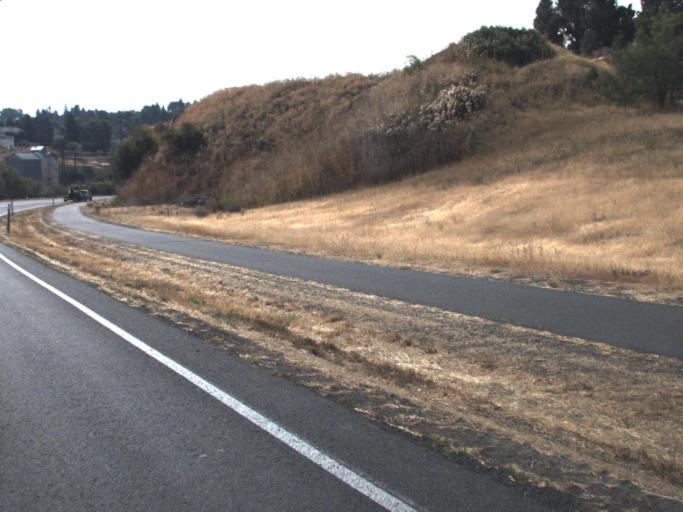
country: US
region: Washington
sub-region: Whitman County
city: Pullman
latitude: 46.7448
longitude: -117.1713
